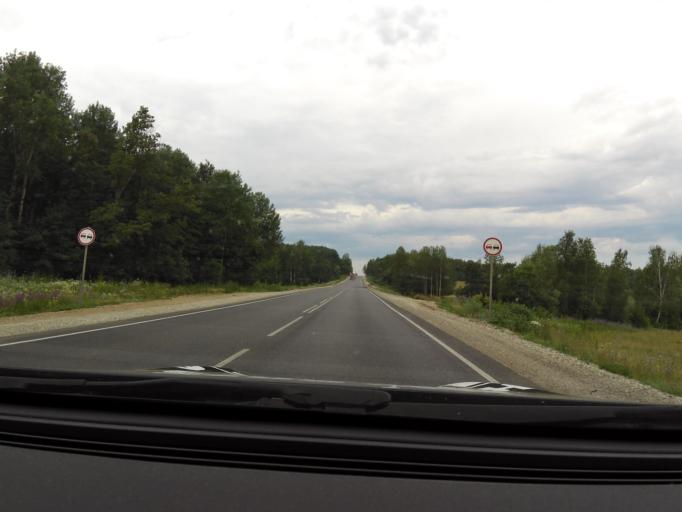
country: RU
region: Bashkortostan
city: Ulu-Telyak
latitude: 54.8446
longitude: 57.0814
